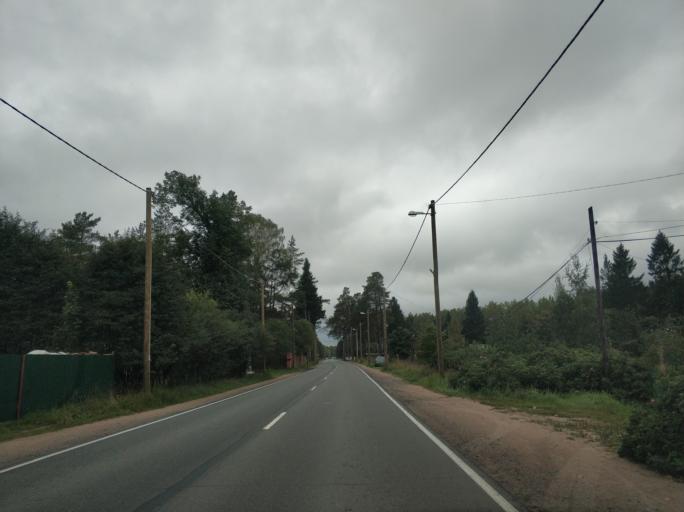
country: RU
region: Leningrad
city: Borisova Griva
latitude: 60.0858
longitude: 30.8822
